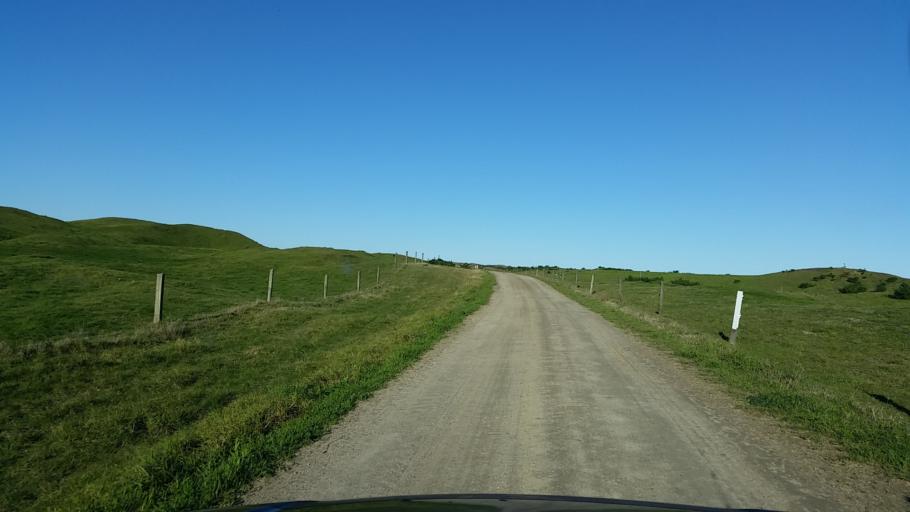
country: NZ
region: Taranaki
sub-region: South Taranaki District
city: Patea
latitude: -39.8371
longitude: 174.6910
